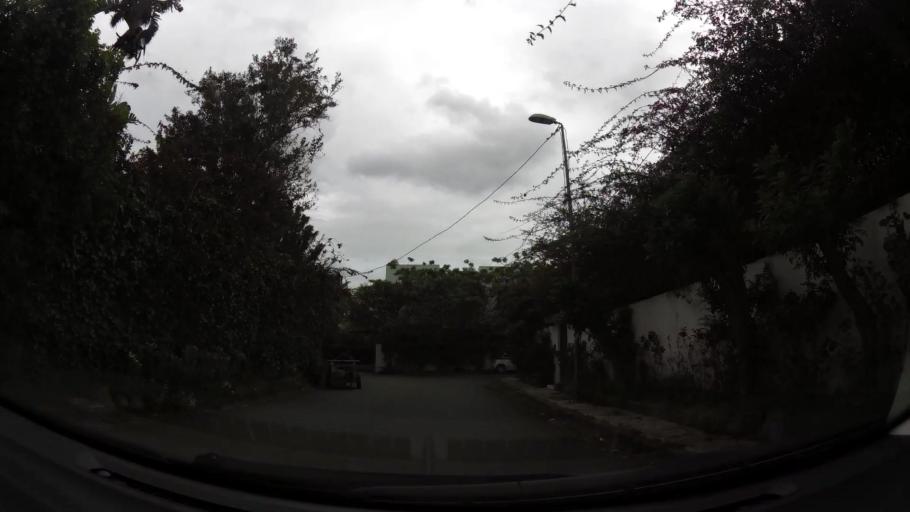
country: MA
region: Grand Casablanca
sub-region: Casablanca
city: Casablanca
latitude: 33.5769
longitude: -7.6611
